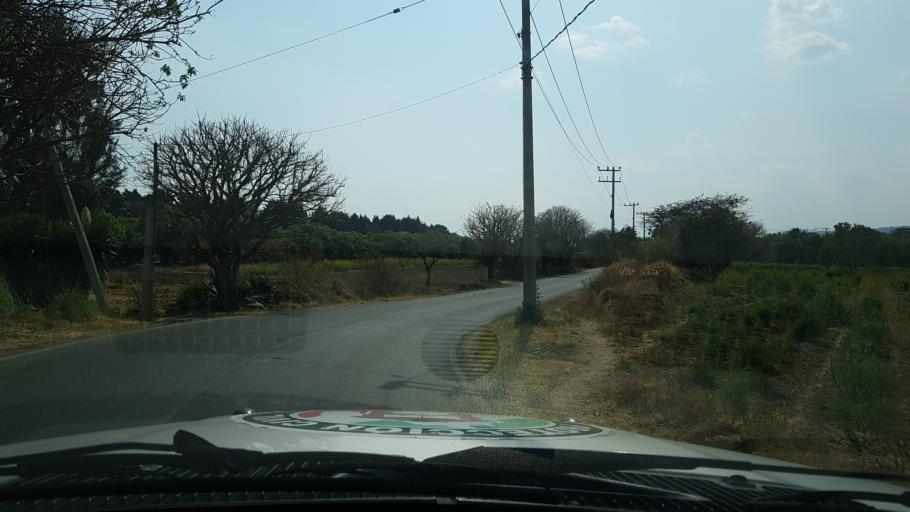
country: MX
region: Mexico
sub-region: Ozumba
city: San Jose Tlacotitlan
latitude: 18.9871
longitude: -98.8136
